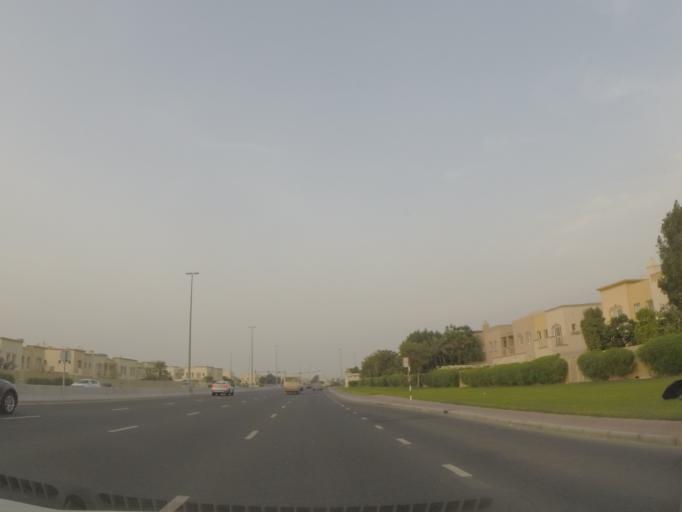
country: AE
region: Dubai
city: Dubai
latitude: 25.0576
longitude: 55.1771
